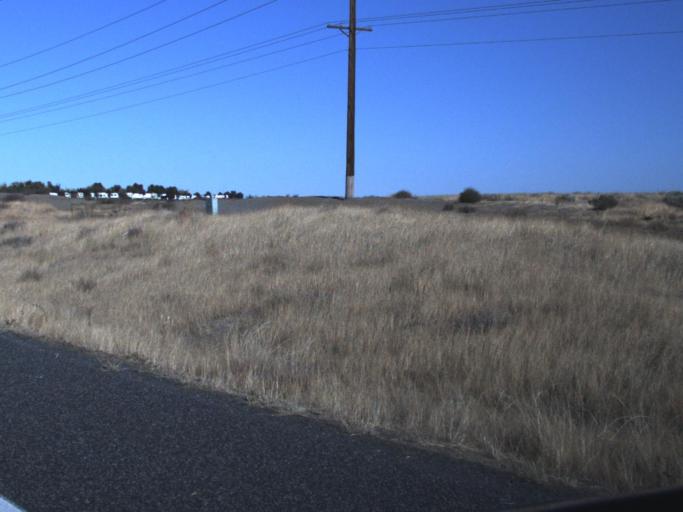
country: US
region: Washington
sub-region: Benton County
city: Richland
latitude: 46.3222
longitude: -119.3097
